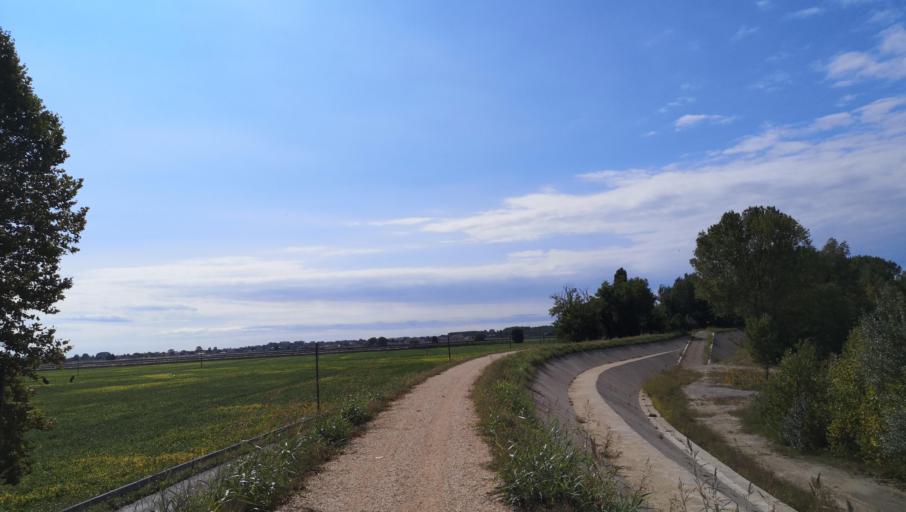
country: IT
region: Friuli Venezia Giulia
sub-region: Provincia di Udine
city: Latisana
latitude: 45.7635
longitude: 13.0135
